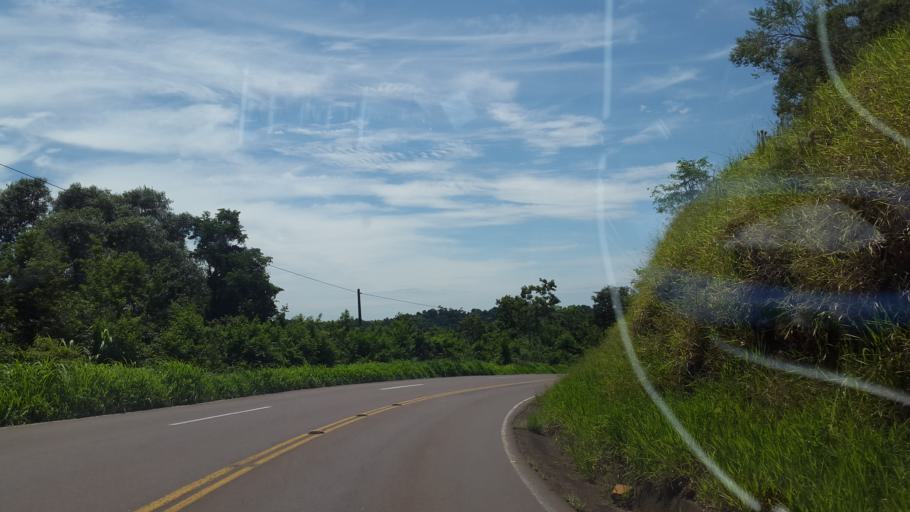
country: BR
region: Rio Grande do Sul
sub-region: Frederico Westphalen
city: Frederico Westphalen
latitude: -27.0653
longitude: -53.4703
